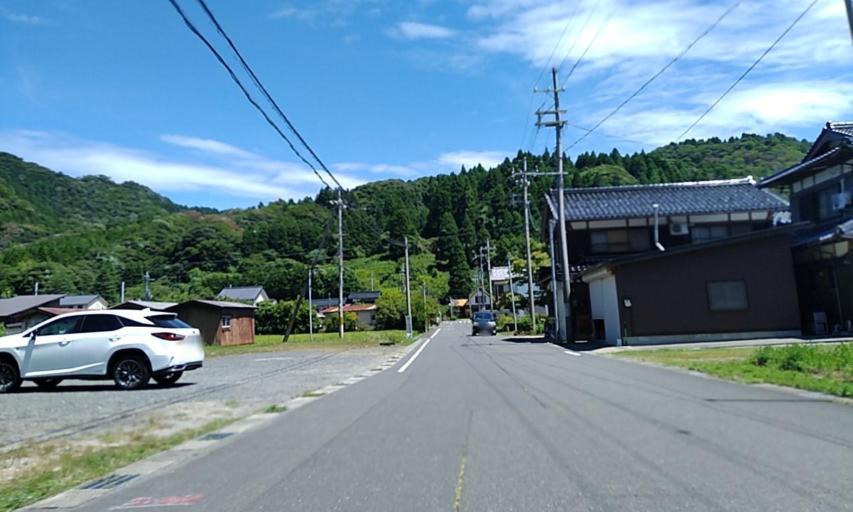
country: JP
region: Kyoto
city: Miyazu
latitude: 35.6713
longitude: 135.2738
